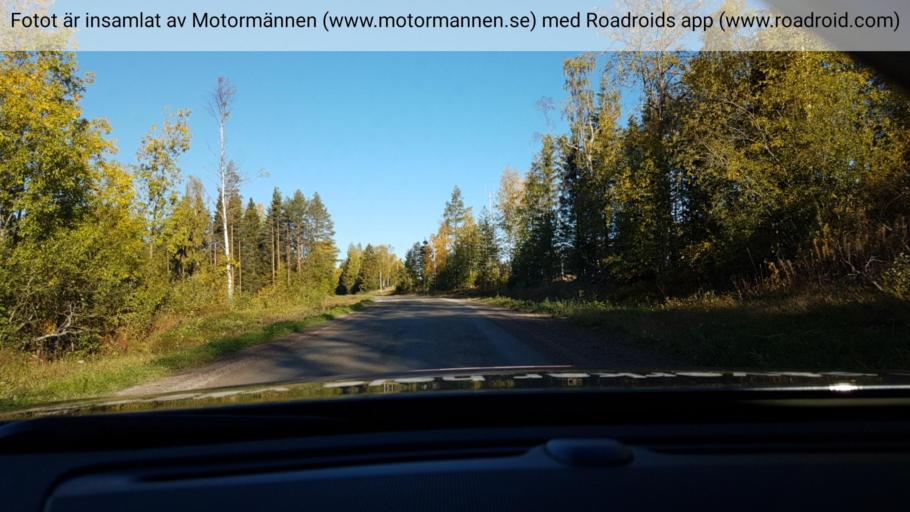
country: SE
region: Norrbotten
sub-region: Alvsbyns Kommun
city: AElvsbyn
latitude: 66.1932
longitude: 21.1929
